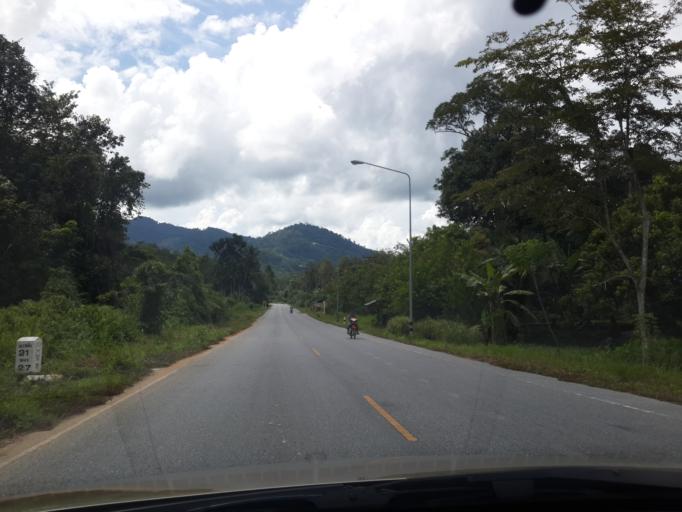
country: TH
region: Yala
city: Raman
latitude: 6.3820
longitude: 101.3969
